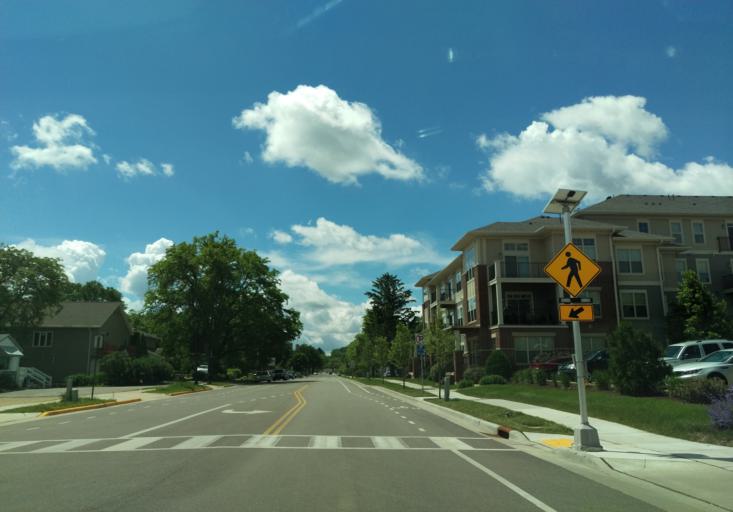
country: US
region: Wisconsin
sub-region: Dane County
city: Middleton
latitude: 43.1013
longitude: -89.5115
